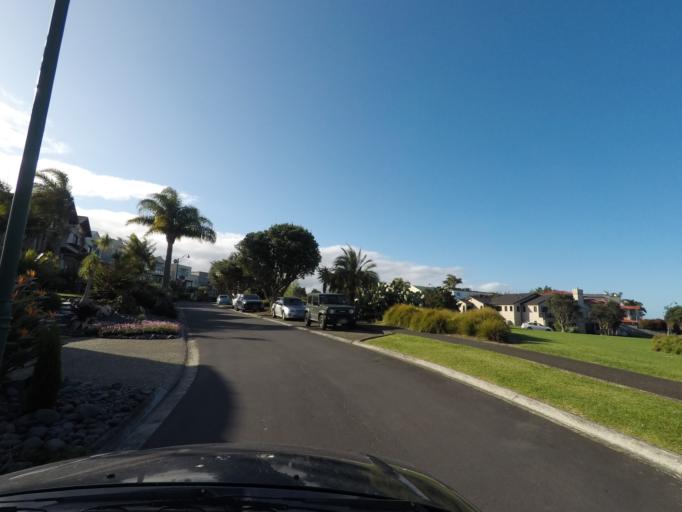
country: NZ
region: Auckland
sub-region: Auckland
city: Rosebank
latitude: -36.8456
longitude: 174.6546
